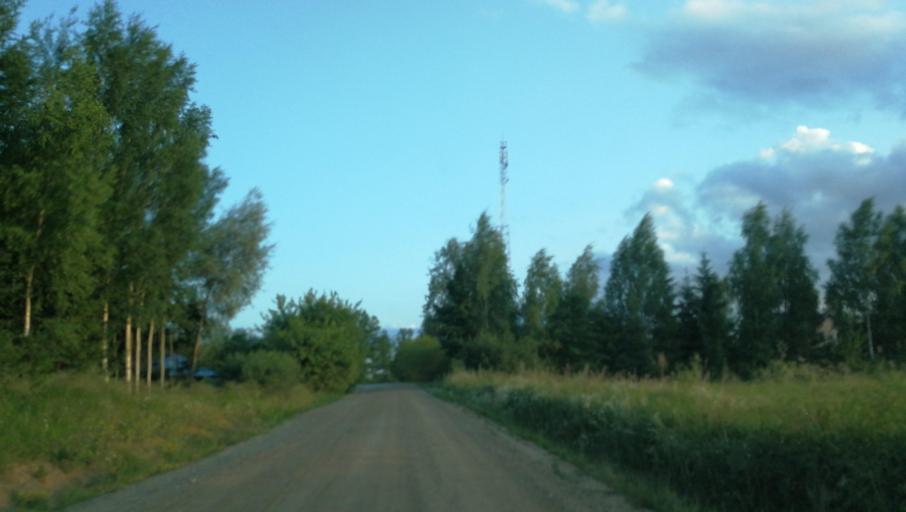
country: LV
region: Amatas Novads
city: Drabesi
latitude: 57.2485
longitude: 25.2152
